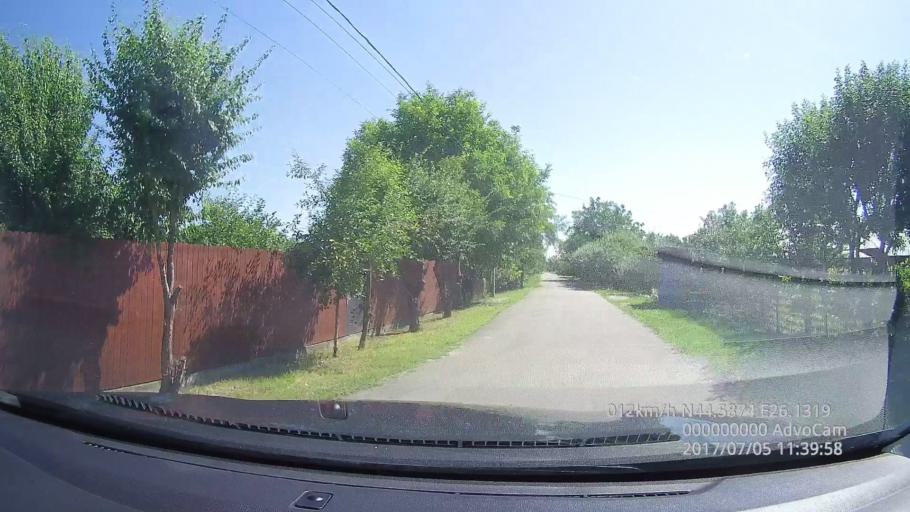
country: RO
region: Ilfov
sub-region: Comuna Balotesti
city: Balotesti
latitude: 44.5874
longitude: 26.1320
